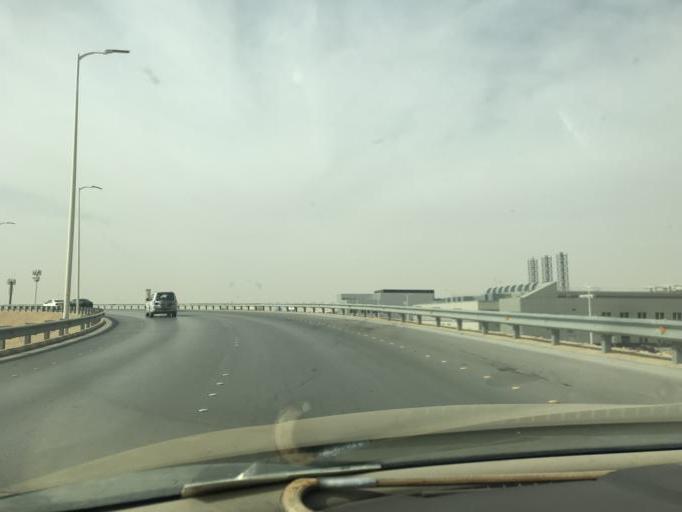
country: SA
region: Ar Riyad
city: Riyadh
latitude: 24.9463
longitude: 46.7084
